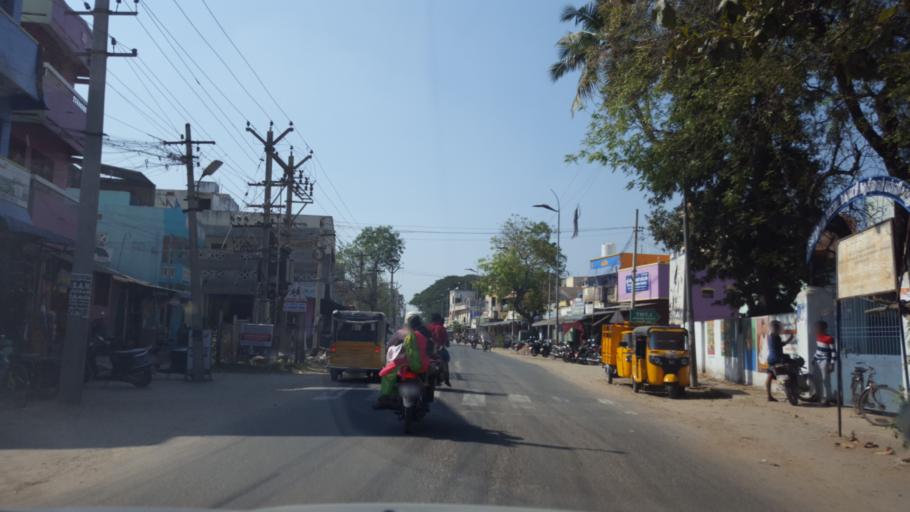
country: IN
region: Tamil Nadu
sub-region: Kancheepuram
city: Kanchipuram
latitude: 12.8509
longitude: 79.6918
